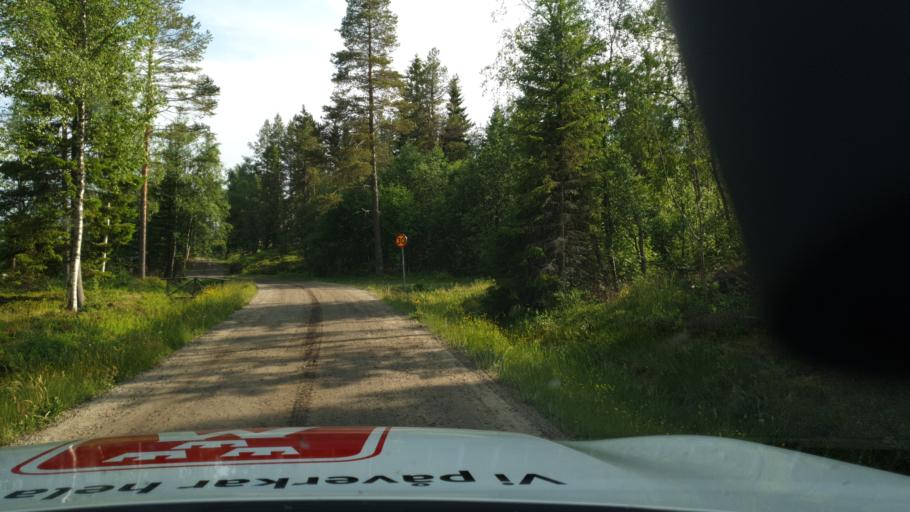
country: SE
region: Vaesterbotten
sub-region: Robertsfors Kommun
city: Robertsfors
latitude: 64.2129
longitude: 21.0780
